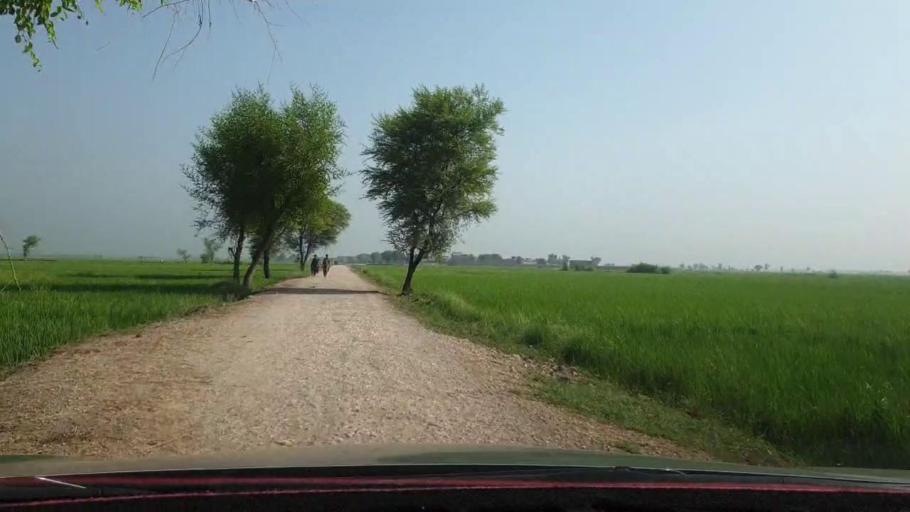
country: PK
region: Sindh
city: Nasirabad
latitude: 27.4707
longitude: 67.9228
